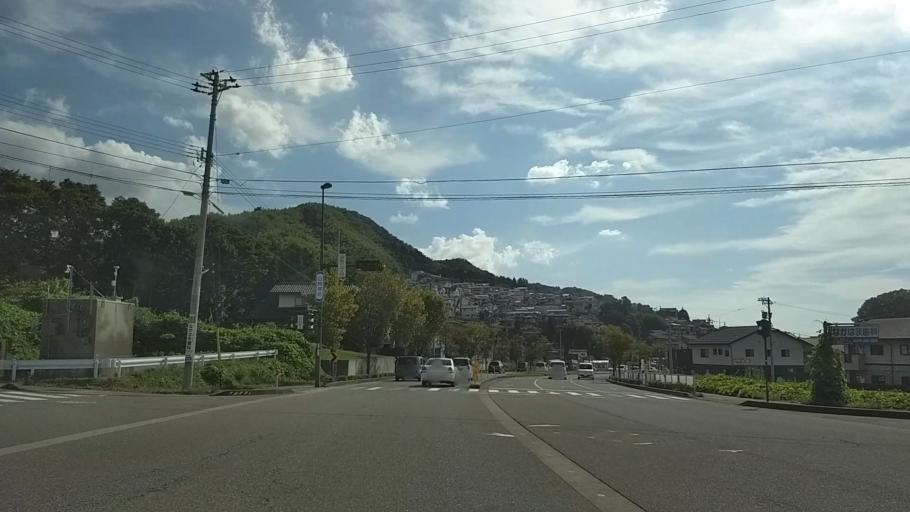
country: JP
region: Ishikawa
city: Nonoichi
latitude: 36.5292
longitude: 136.6520
